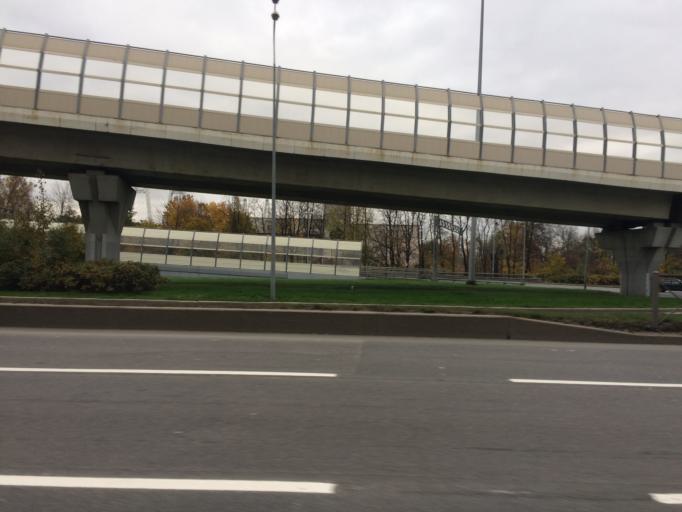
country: RU
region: Leningrad
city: Rybatskoye
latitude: 59.8516
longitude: 30.4801
